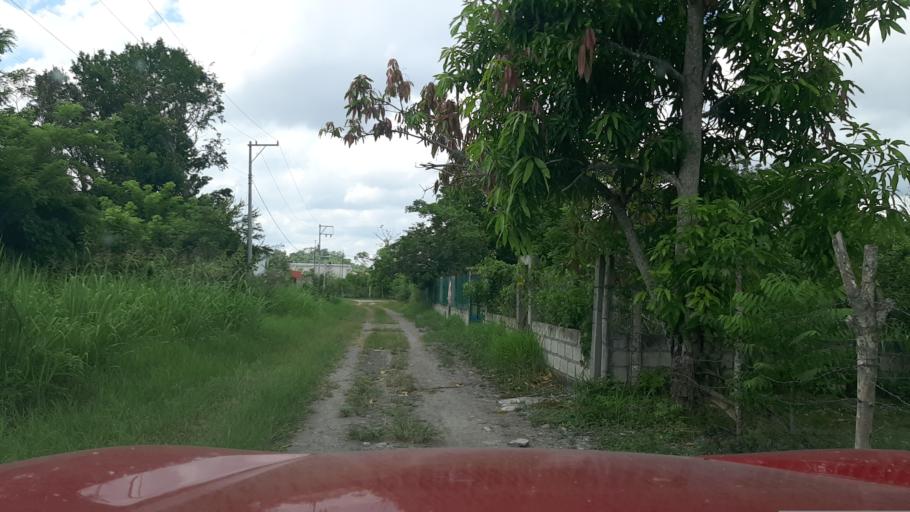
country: MX
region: Veracruz
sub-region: Poza Rica de Hidalgo
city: Villa de las Flores
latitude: 20.5725
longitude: -97.4354
